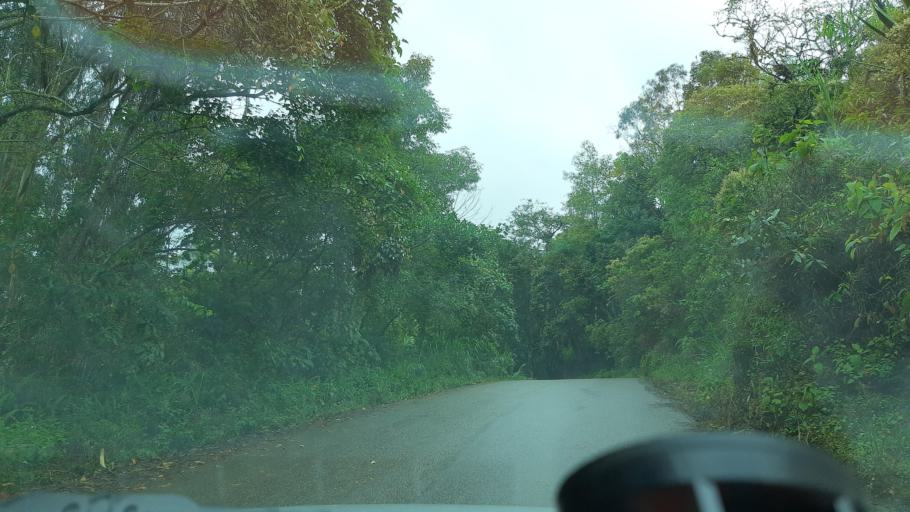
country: CO
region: Cundinamarca
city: Manta
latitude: 5.0475
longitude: -73.5101
